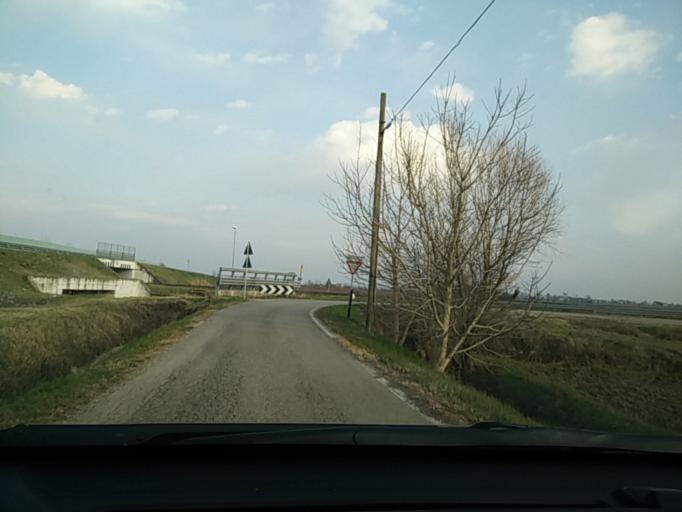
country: IT
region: Veneto
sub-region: Provincia di Venezia
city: Musile di Piave
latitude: 45.6064
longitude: 12.5108
